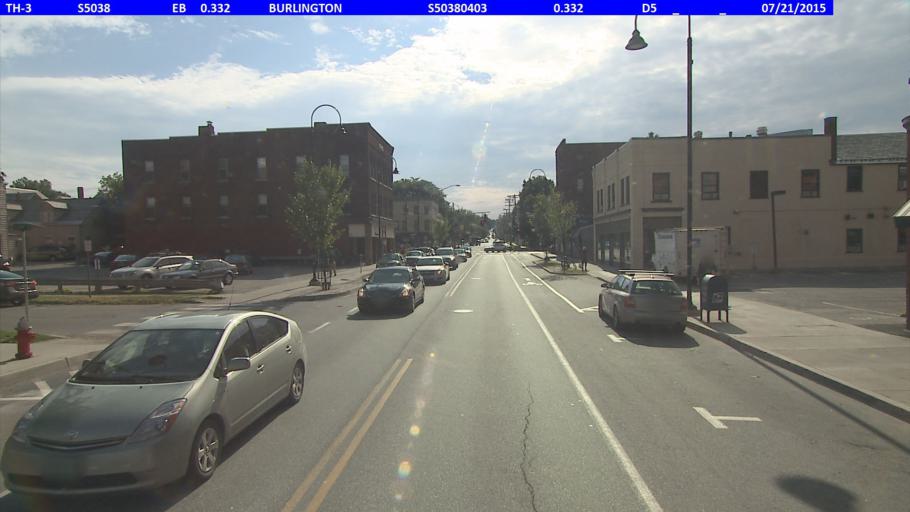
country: US
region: Vermont
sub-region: Chittenden County
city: Burlington
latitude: 44.4804
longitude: -73.2125
